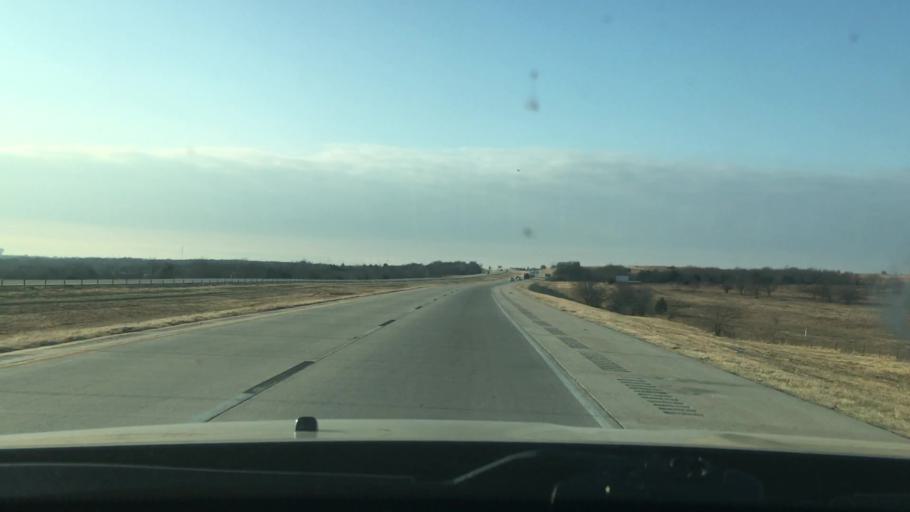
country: US
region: Oklahoma
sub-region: Carter County
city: Ardmore
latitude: 34.2315
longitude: -97.1618
